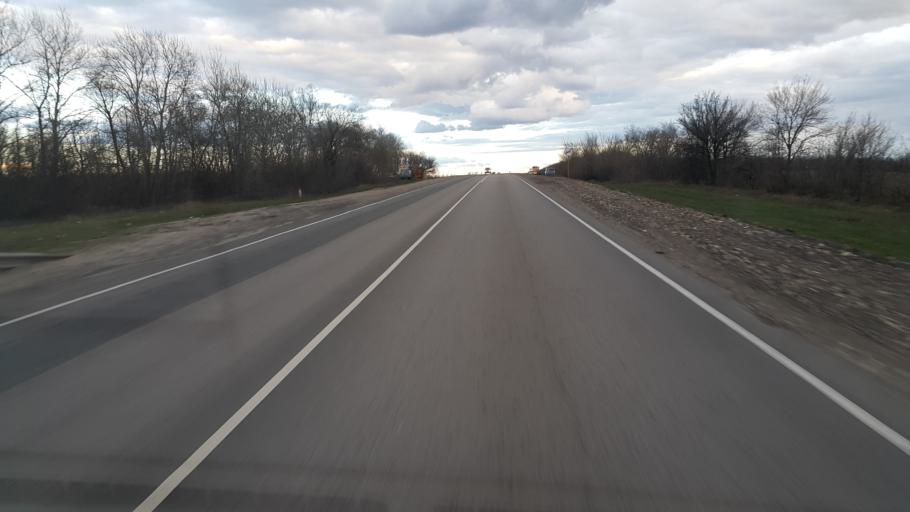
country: RU
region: Volgograd
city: Mikhaylovka
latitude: 49.9895
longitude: 43.2590
